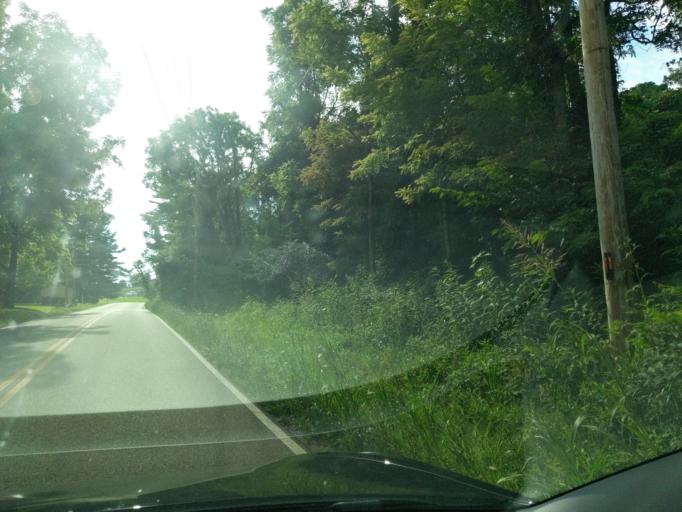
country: US
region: Ohio
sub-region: Fairfield County
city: Lancaster
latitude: 39.5646
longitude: -82.5979
